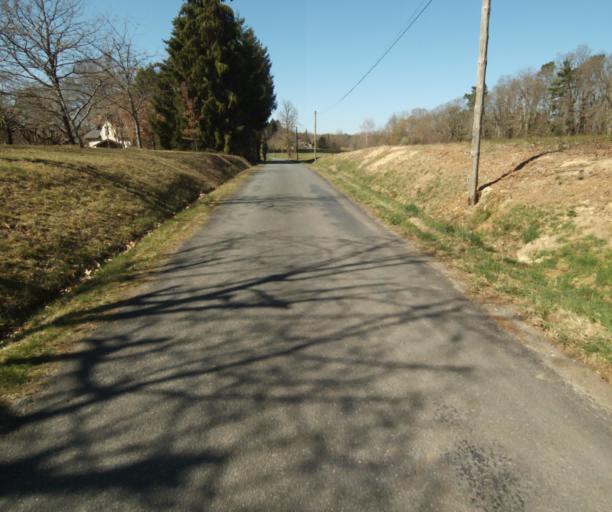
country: FR
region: Limousin
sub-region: Departement de la Correze
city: Chameyrat
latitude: 45.2837
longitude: 1.7131
